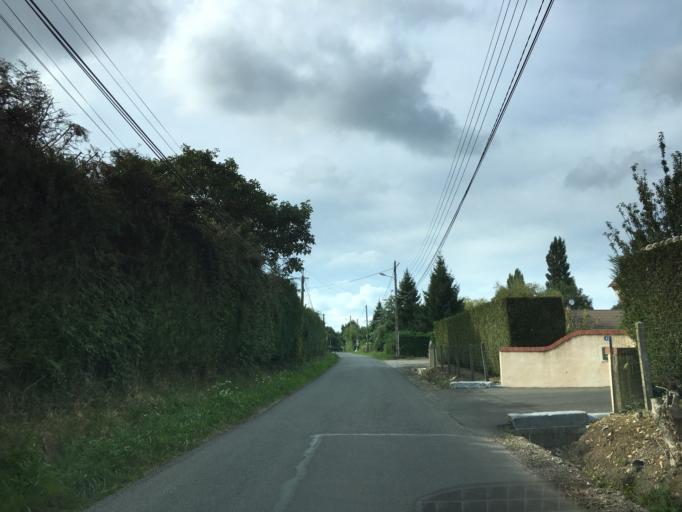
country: FR
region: Lower Normandy
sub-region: Departement du Calvados
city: Villers-sur-Mer
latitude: 49.3076
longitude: -0.0310
